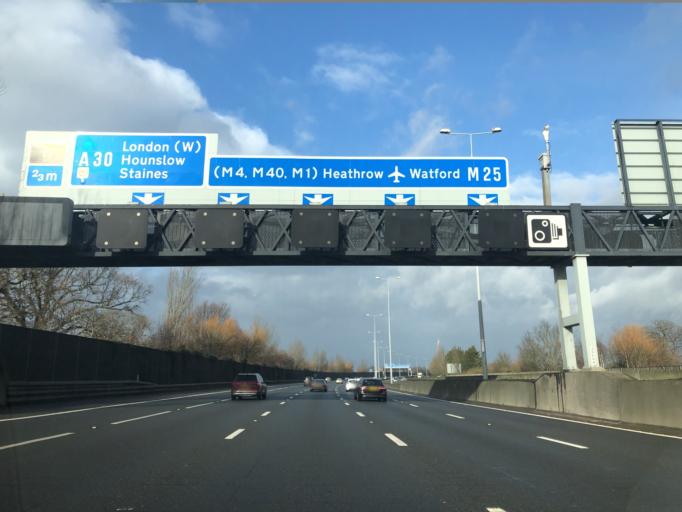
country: GB
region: England
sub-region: Surrey
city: Egham
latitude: 51.4250
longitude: -0.5409
